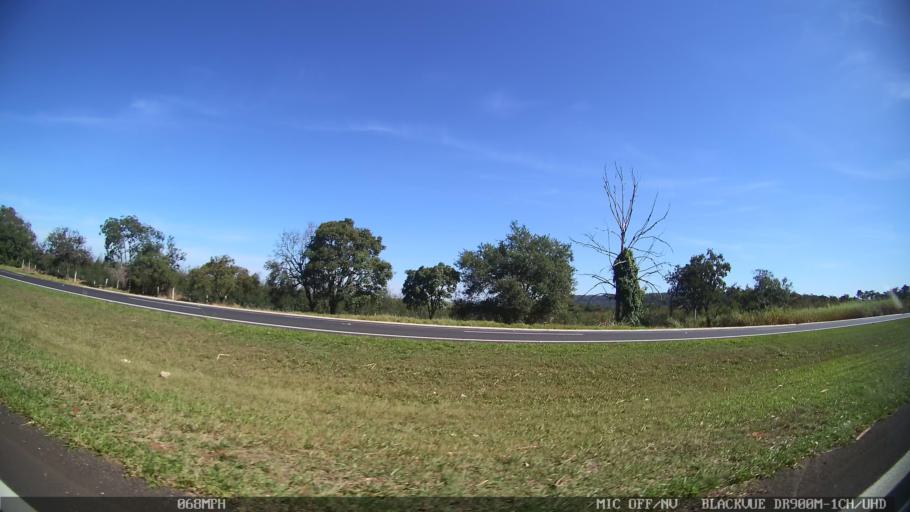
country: BR
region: Sao Paulo
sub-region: Sao Simao
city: Sao Simao
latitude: -21.5574
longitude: -47.6359
